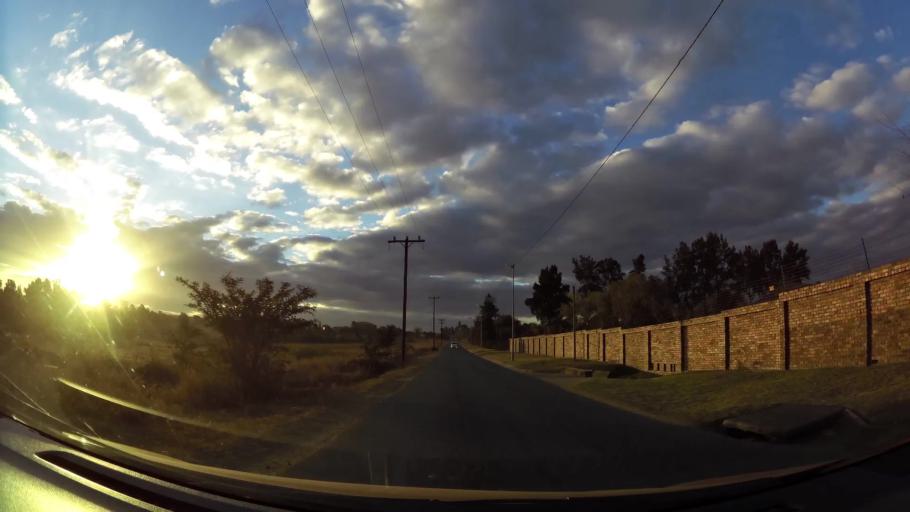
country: ZA
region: Gauteng
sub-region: City of Johannesburg Metropolitan Municipality
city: Midrand
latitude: -26.0008
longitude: 28.1513
